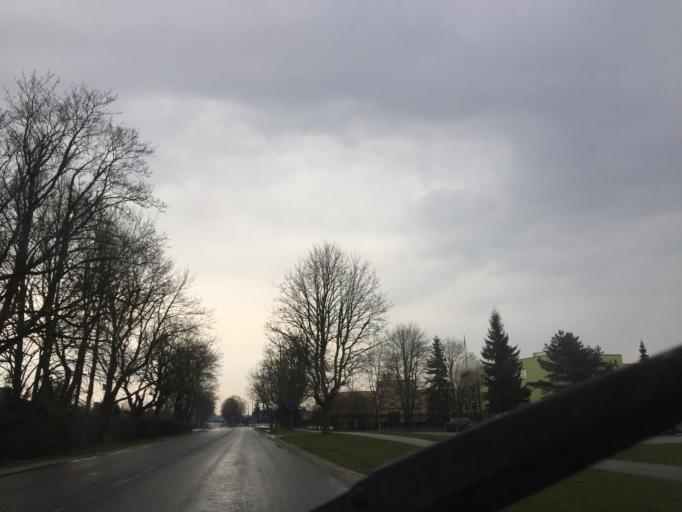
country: EE
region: Tartu
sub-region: UElenurme vald
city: Ulenurme
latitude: 58.3204
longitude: 26.7213
